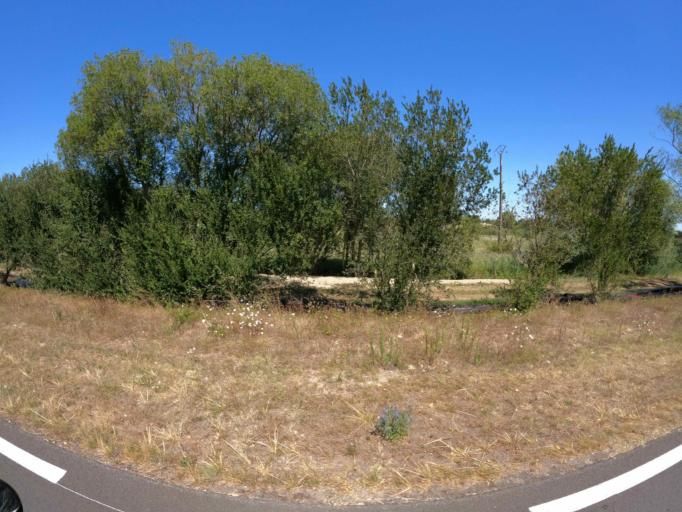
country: FR
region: Pays de la Loire
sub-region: Departement de la Vendee
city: Saint-Jean-de-Monts
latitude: 46.7975
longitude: -2.0520
